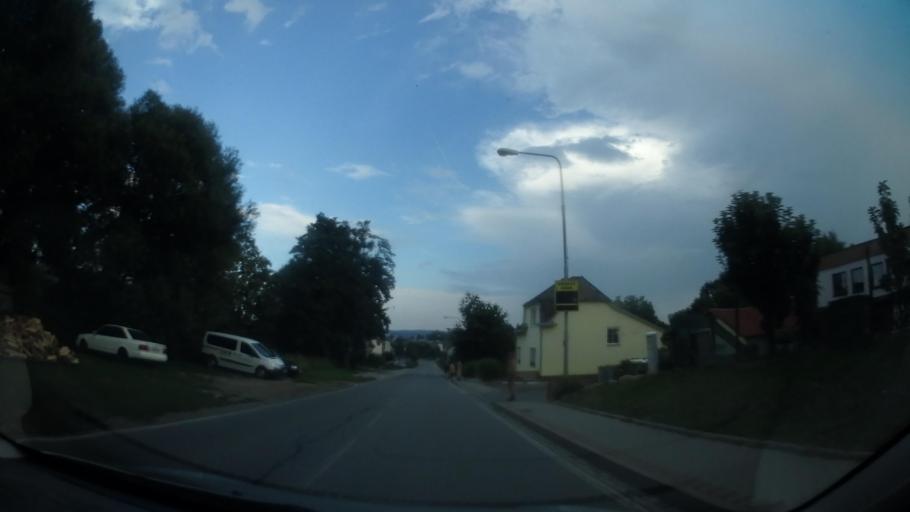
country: CZ
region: Olomoucky
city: Zabreh
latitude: 49.8866
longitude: 16.8510
